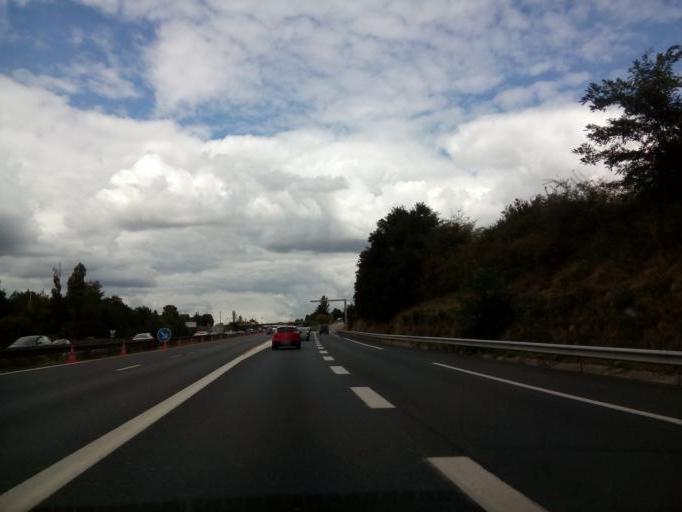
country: FR
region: Rhone-Alpes
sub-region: Departement du Rhone
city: Dardilly
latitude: 45.8168
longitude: 4.7658
